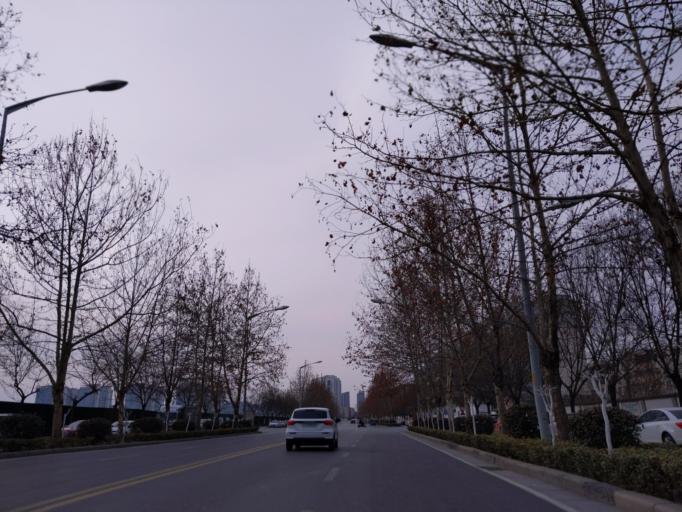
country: CN
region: Henan Sheng
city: Zhongyuanlu
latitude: 35.7581
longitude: 115.0495
